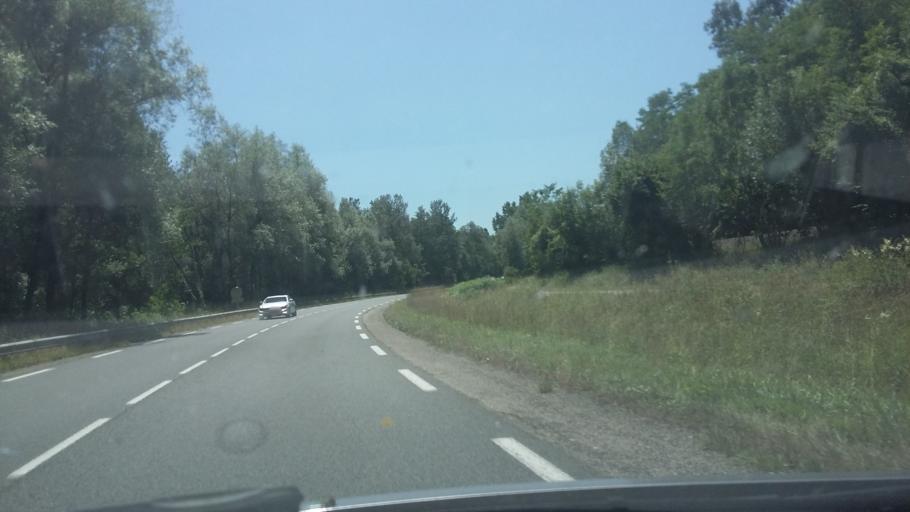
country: FR
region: Rhone-Alpes
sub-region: Departement de l'Ain
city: Belley
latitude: 45.7758
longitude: 5.7131
